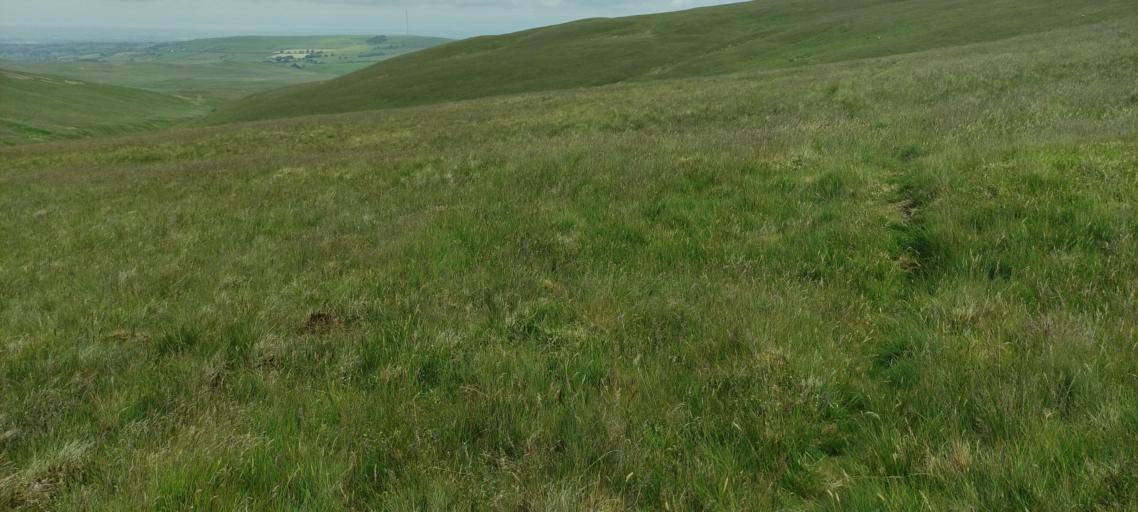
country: GB
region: England
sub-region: Cumbria
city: Keswick
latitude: 54.7022
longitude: -3.1120
